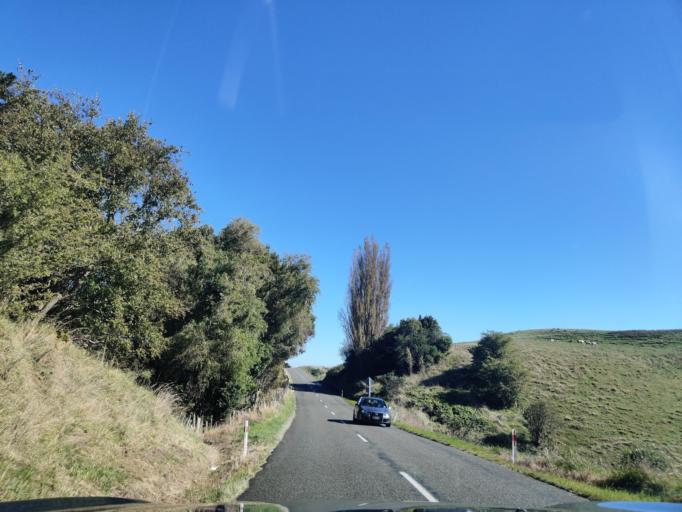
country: NZ
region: Manawatu-Wanganui
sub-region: Palmerston North City
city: Palmerston North
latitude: -40.2591
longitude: 175.7117
